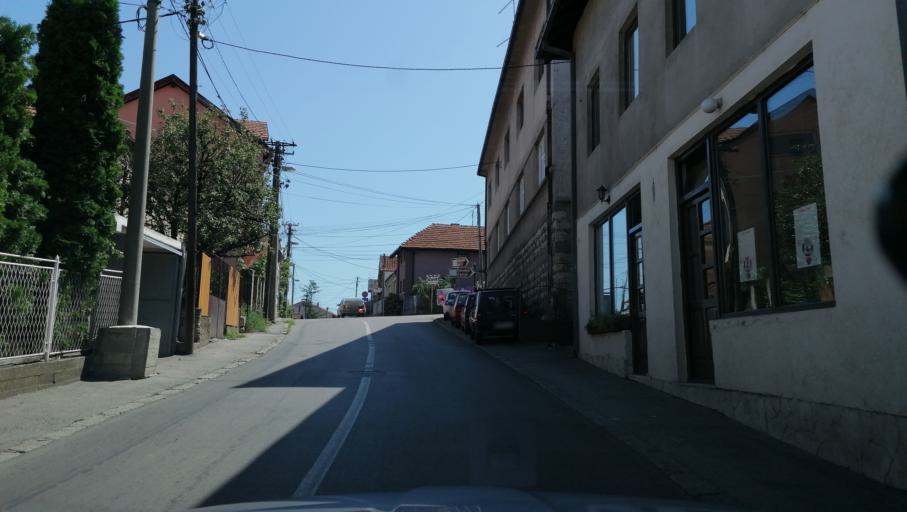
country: RS
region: Central Serbia
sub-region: Kolubarski Okrug
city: Valjevo
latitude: 44.2675
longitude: 19.8816
